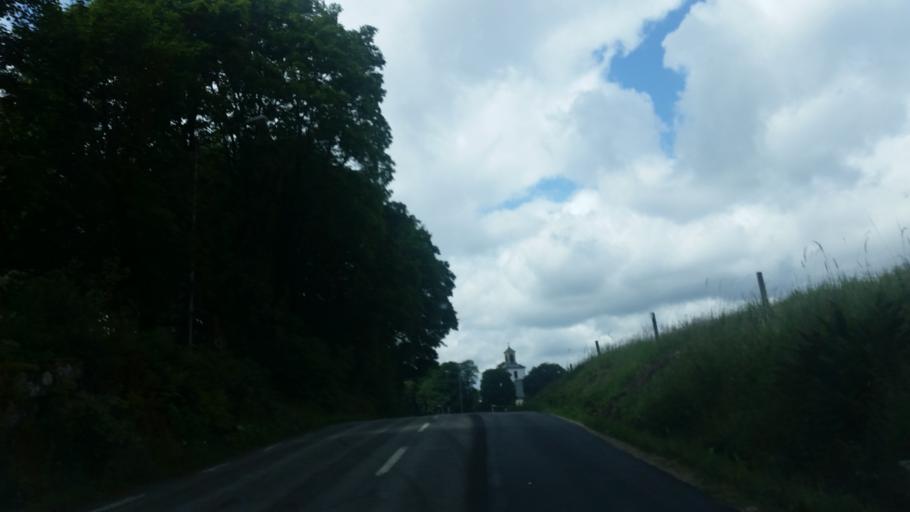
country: SE
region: Joenkoeping
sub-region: Gislaveds Kommun
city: Reftele
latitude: 57.1796
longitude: 13.5720
